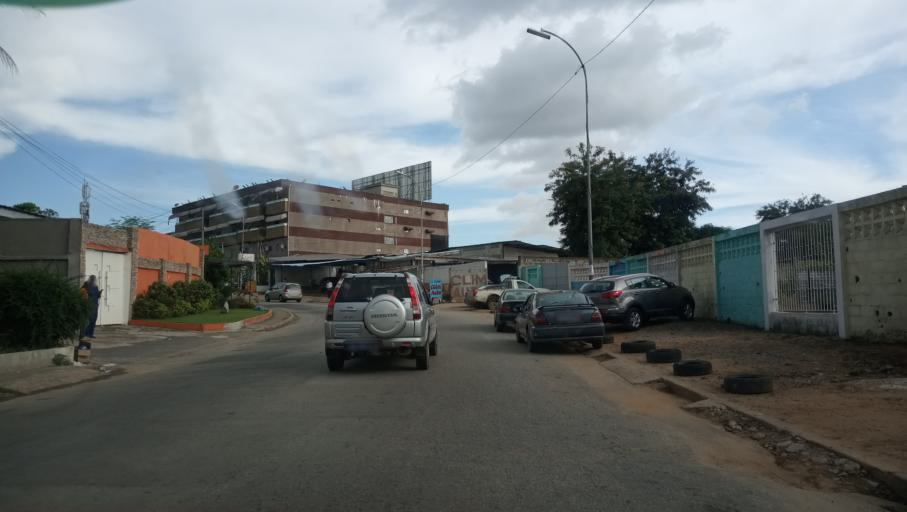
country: CI
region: Lagunes
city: Abidjan
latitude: 5.3503
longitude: -3.9815
